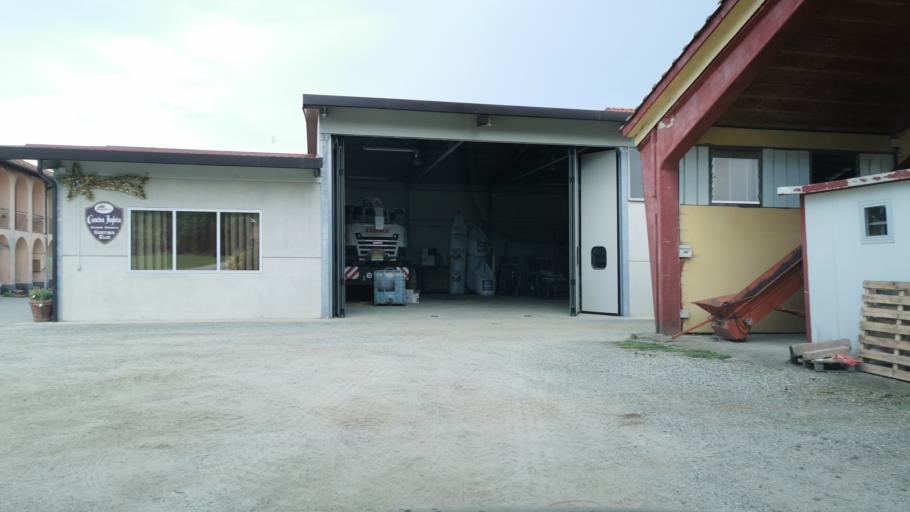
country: IT
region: Piedmont
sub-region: Provincia di Torino
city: Barbania
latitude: 45.3034
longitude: 7.6422
